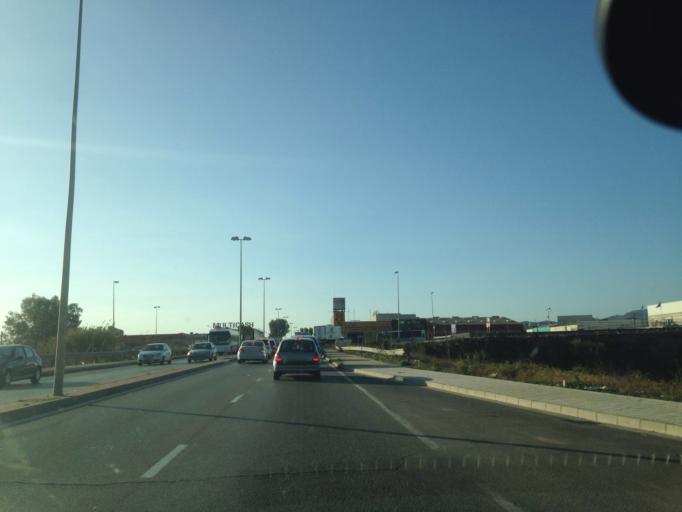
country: ES
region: Andalusia
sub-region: Provincia de Malaga
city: Malaga
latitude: 36.7153
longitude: -4.4831
